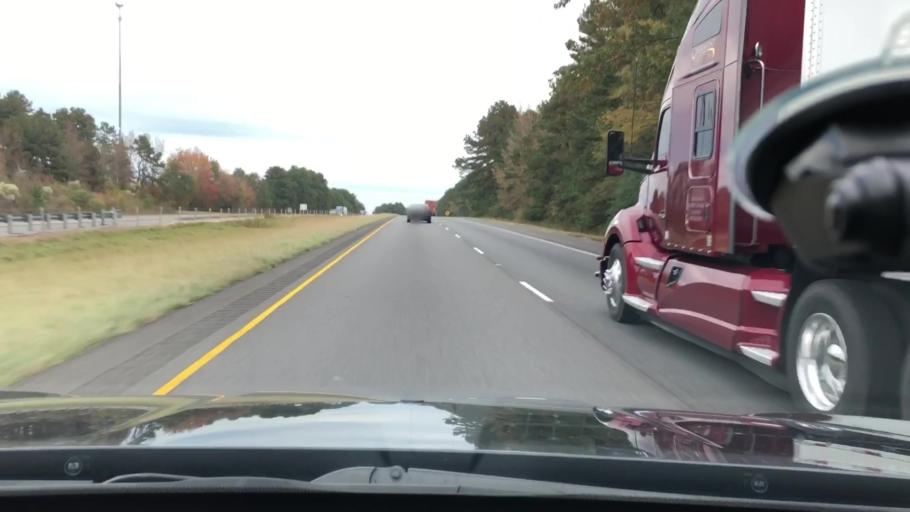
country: US
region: Arkansas
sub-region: Clark County
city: Arkadelphia
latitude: 34.2355
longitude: -93.0070
